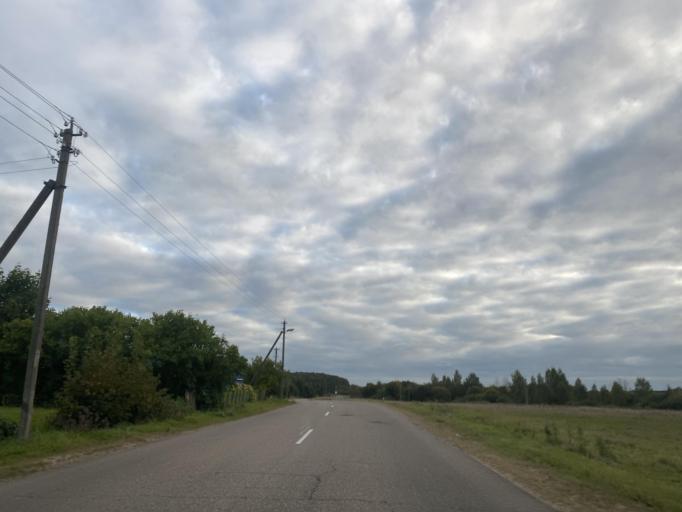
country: BY
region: Grodnenskaya
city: Kreva
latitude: 54.3022
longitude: 26.2770
